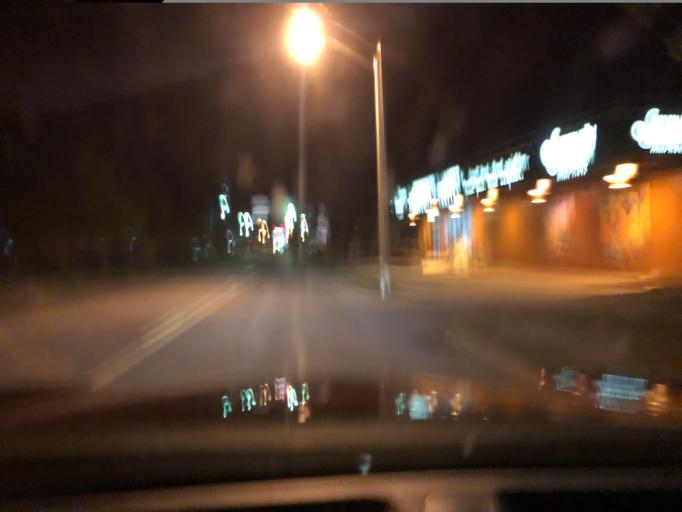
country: US
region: Ohio
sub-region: Logan County
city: Bellefontaine
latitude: 40.3650
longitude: -83.7594
